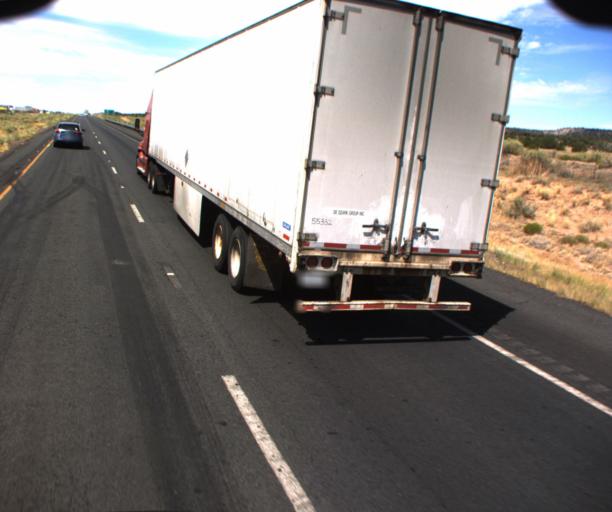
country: US
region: Arizona
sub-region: Apache County
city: Houck
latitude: 35.3053
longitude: -109.1192
